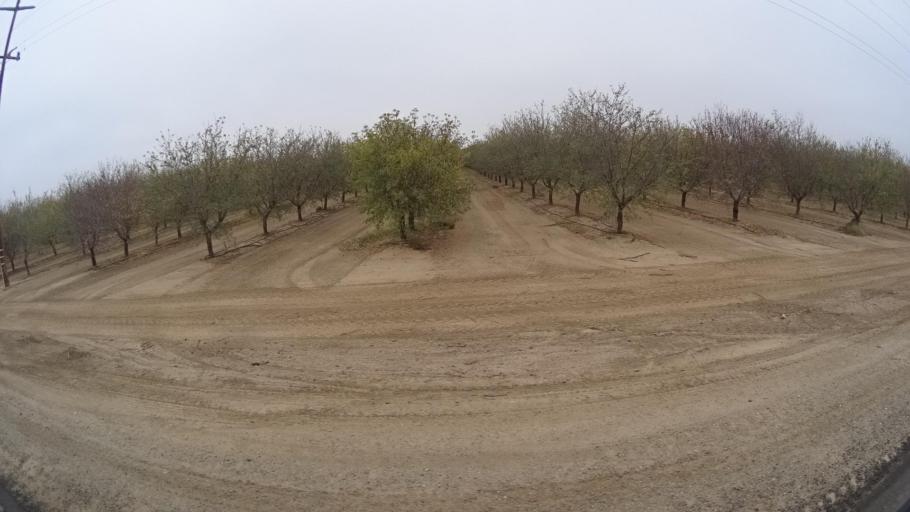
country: US
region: California
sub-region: Kern County
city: Maricopa
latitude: 35.0939
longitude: -119.3075
